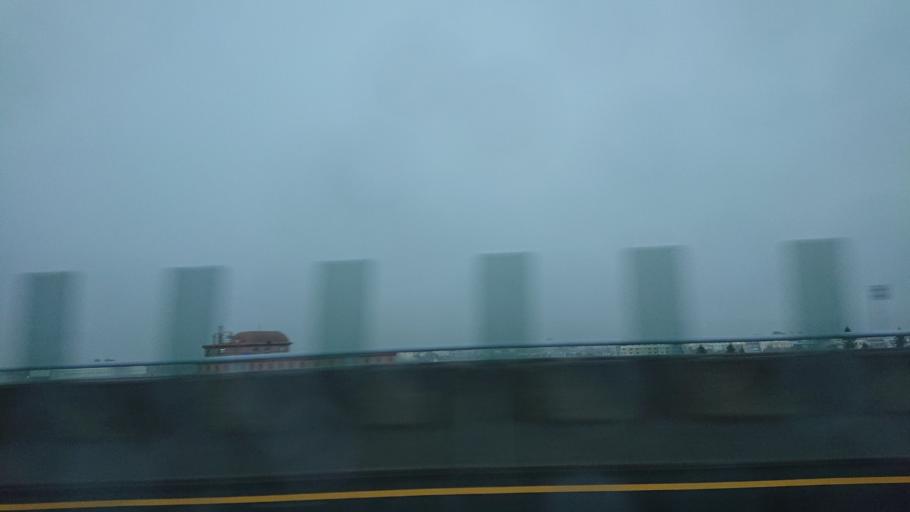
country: TW
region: Taiwan
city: Fengyuan
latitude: 24.2848
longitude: 120.5498
